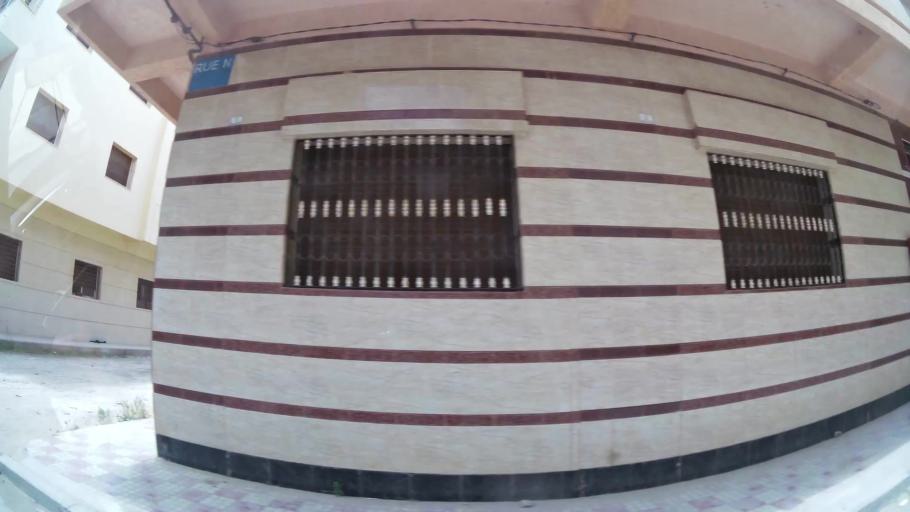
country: MA
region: Oriental
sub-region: Nador
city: Nador
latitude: 35.1639
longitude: -2.9224
